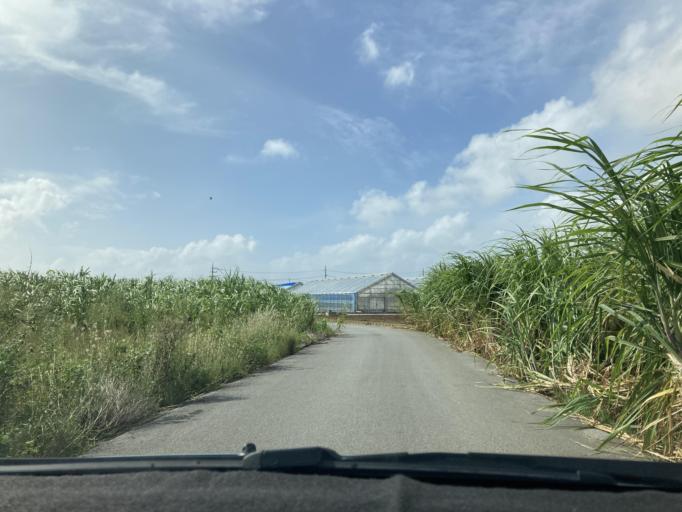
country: JP
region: Okinawa
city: Itoman
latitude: 26.0914
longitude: 127.7049
